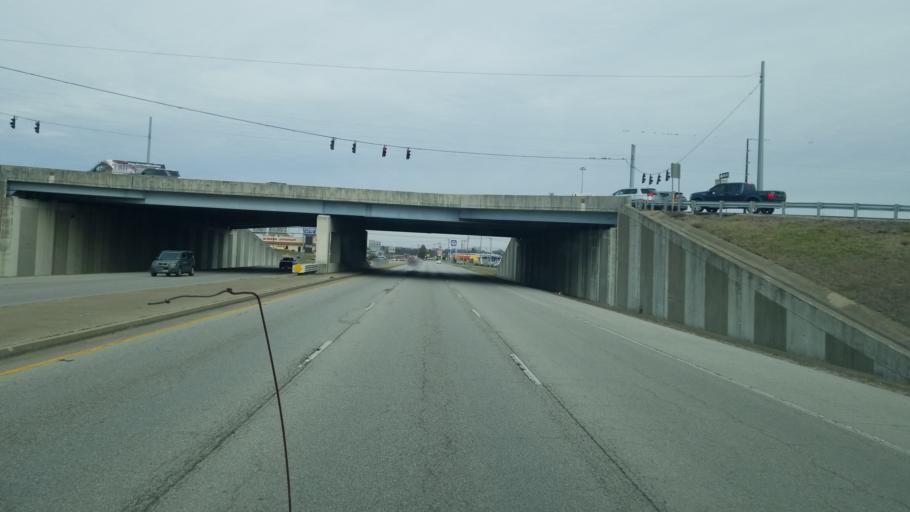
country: US
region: Kentucky
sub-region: Fayette County
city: Lexington-Fayette
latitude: 38.0421
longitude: -84.4542
